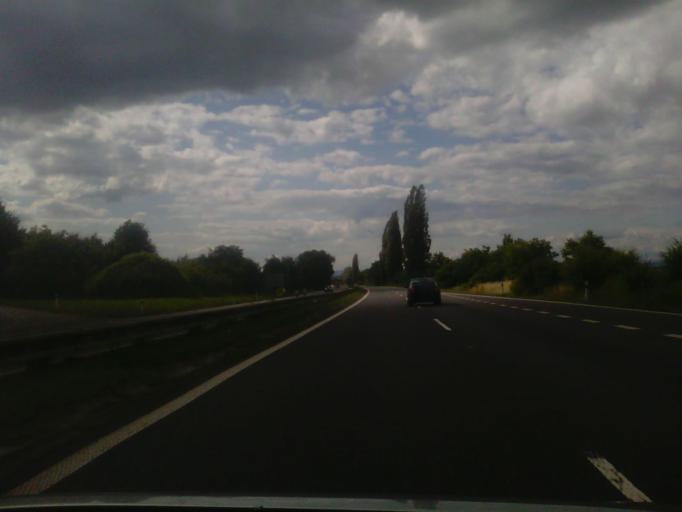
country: CZ
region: Olomoucky
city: Skrben
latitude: 49.6138
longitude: 17.1900
